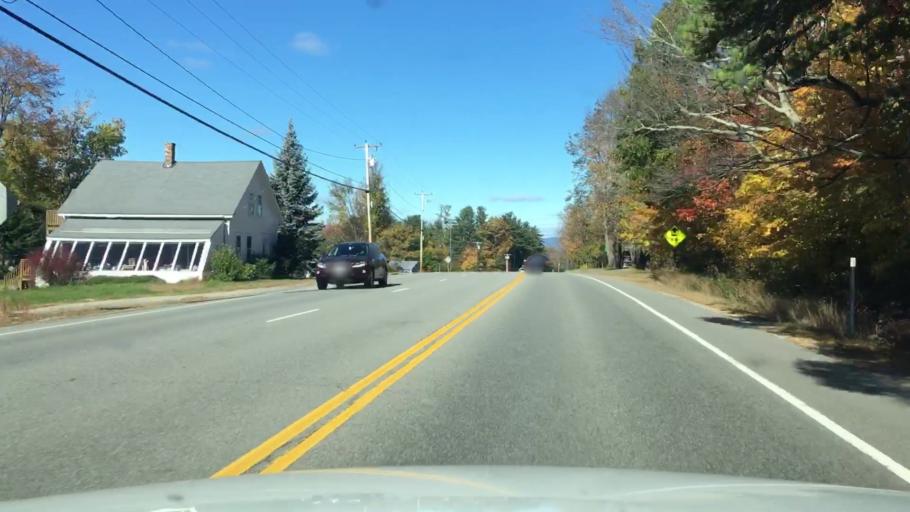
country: US
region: New Hampshire
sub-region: Carroll County
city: Ossipee
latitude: 43.7302
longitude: -71.1274
